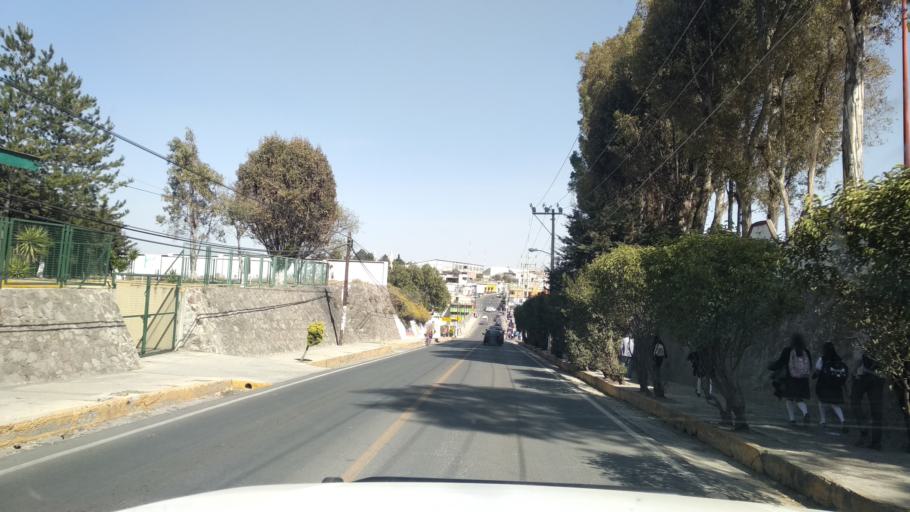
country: MX
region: Hidalgo
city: Calpulalpan
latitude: 19.5889
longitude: -98.5760
